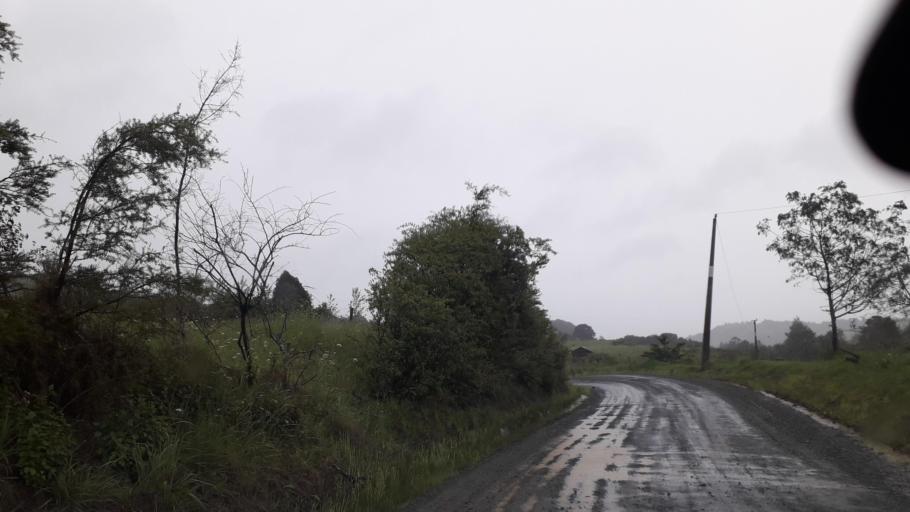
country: NZ
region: Northland
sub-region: Far North District
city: Kerikeri
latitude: -35.1324
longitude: 173.7387
